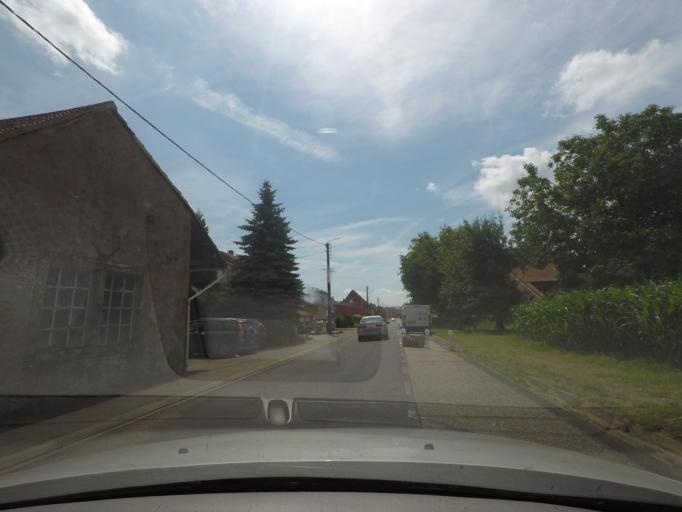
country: FR
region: Alsace
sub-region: Departement du Bas-Rhin
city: Drulingen
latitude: 48.8328
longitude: 7.2322
